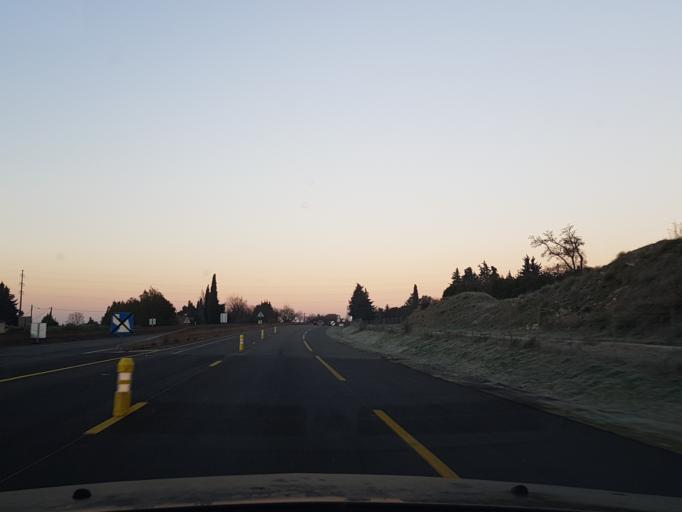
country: FR
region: Provence-Alpes-Cote d'Azur
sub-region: Departement du Vaucluse
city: Monteux
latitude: 44.0450
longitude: 5.0176
